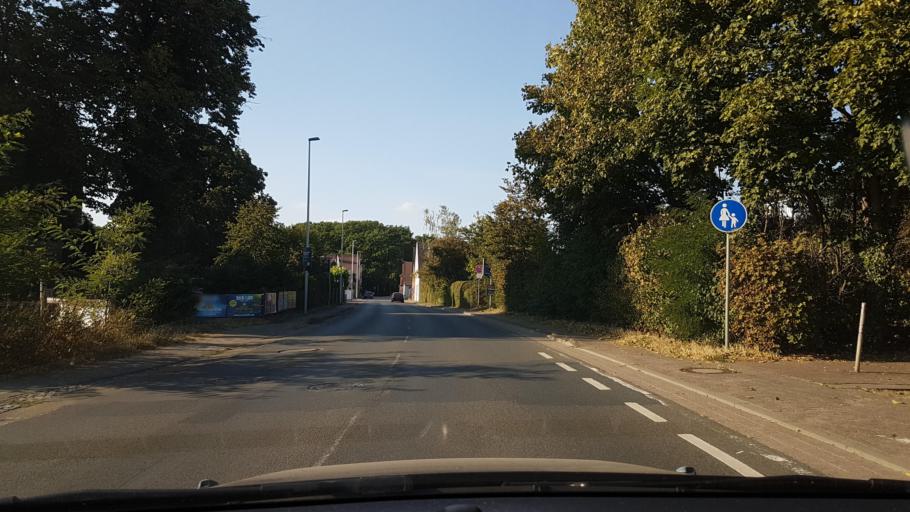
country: DE
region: Lower Saxony
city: Hagenburg
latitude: 52.4501
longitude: 9.3567
